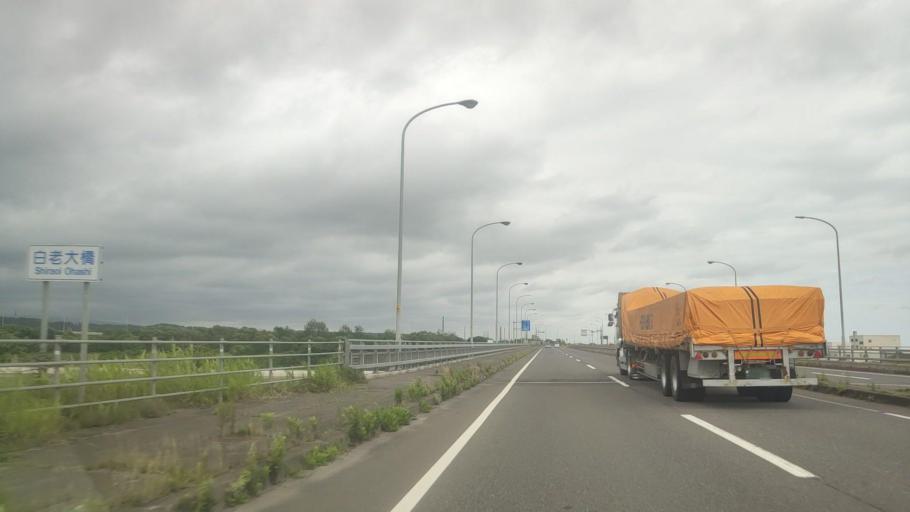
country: JP
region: Hokkaido
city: Shiraoi
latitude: 42.5420
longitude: 141.3445
